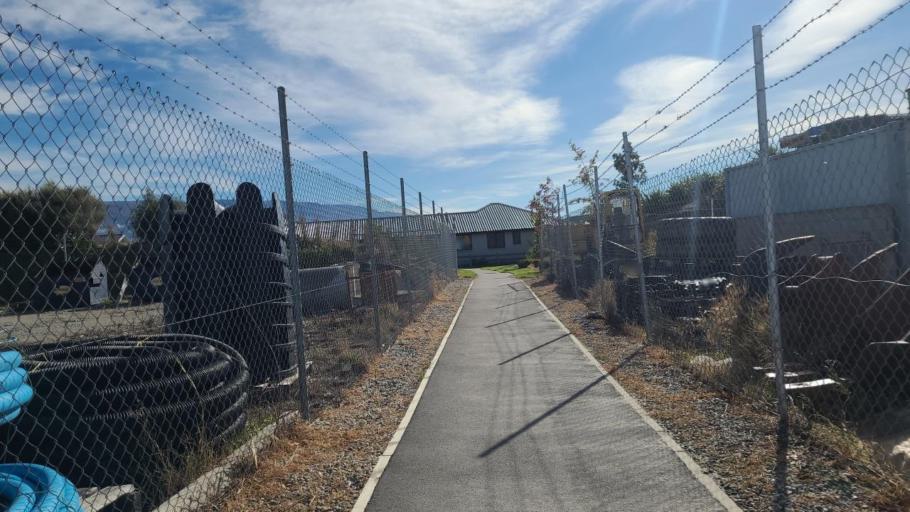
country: NZ
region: Otago
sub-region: Queenstown-Lakes District
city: Wanaka
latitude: -45.0491
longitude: 169.1894
